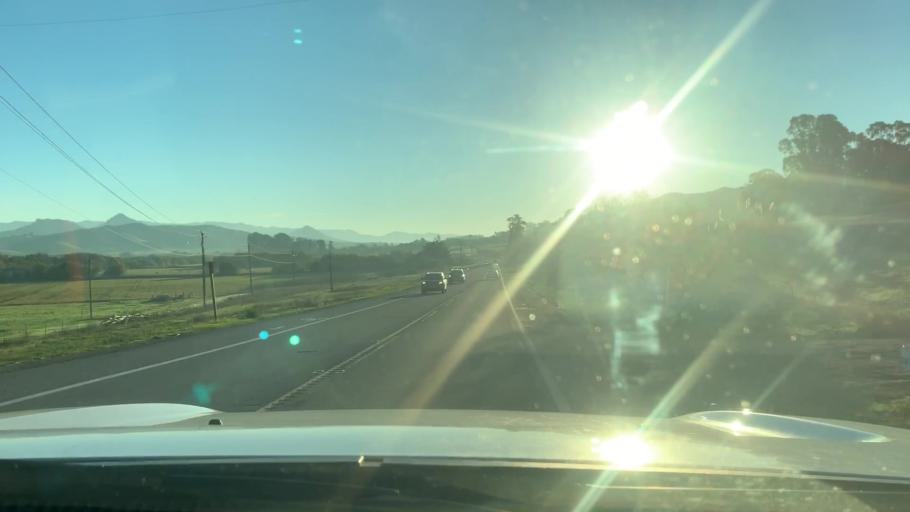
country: US
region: California
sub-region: San Luis Obispo County
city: Los Osos
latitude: 35.3017
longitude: -120.7932
